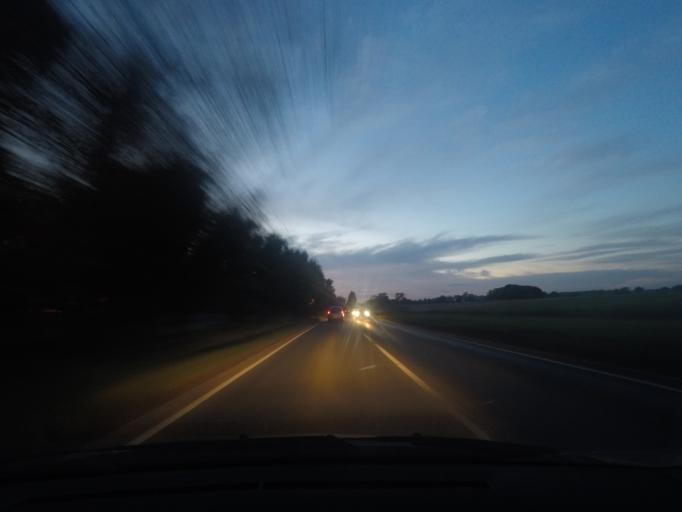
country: GB
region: England
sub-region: East Riding of Yorkshire
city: Wilberfoss
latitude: 53.9491
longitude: -0.9025
